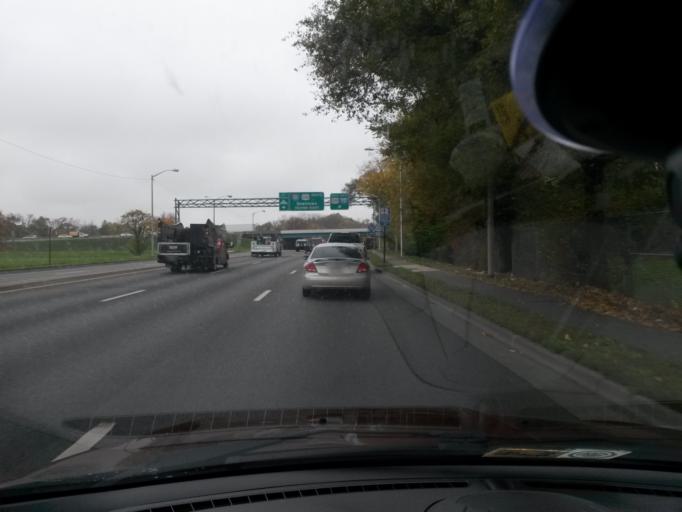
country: US
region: Virginia
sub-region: City of Roanoke
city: Roanoke
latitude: 37.2824
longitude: -79.9361
